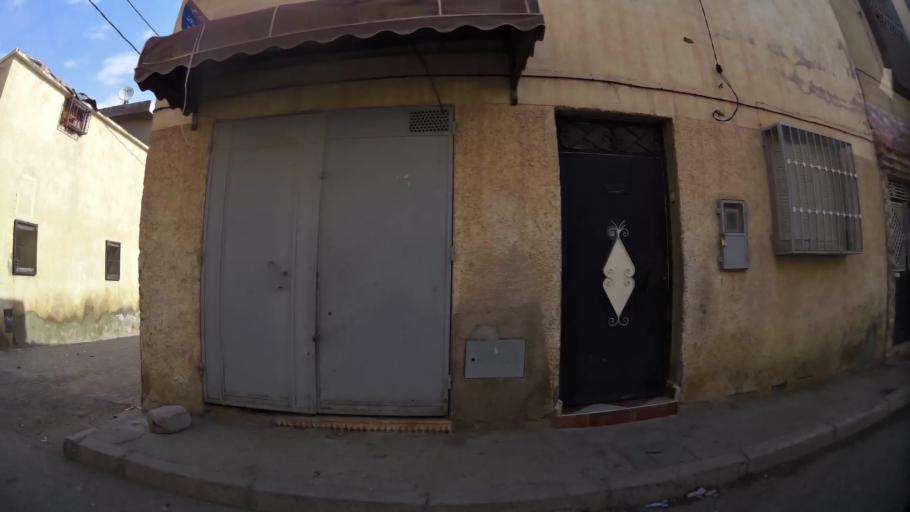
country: MA
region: Oriental
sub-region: Oujda-Angad
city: Oujda
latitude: 34.6884
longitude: -1.8986
